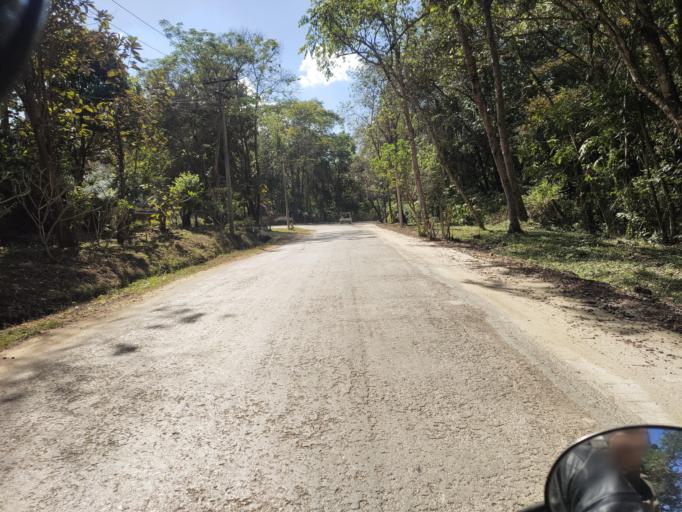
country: MM
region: Mandalay
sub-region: Pyin Oo Lwin District
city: Pyin Oo Lwin
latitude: 21.9883
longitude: 96.4697
